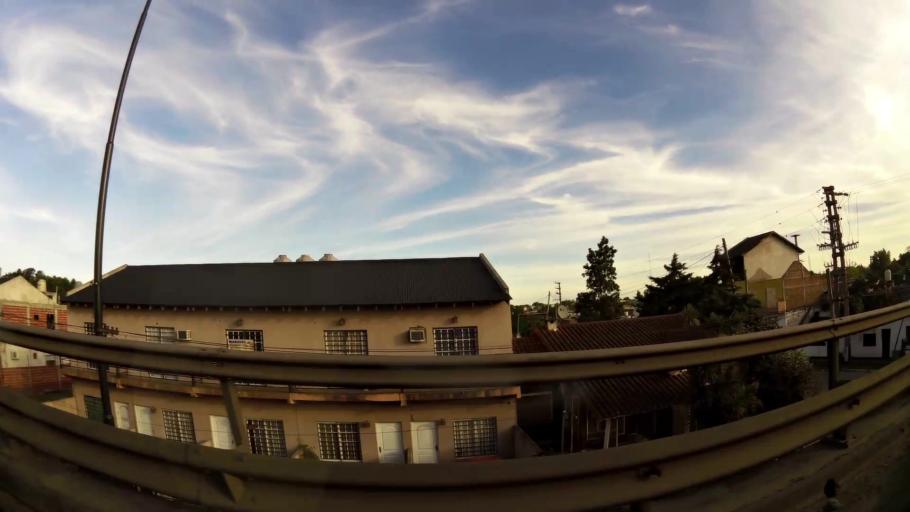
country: AR
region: Buenos Aires
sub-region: Partido de Almirante Brown
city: Adrogue
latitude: -34.8038
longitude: -58.3343
